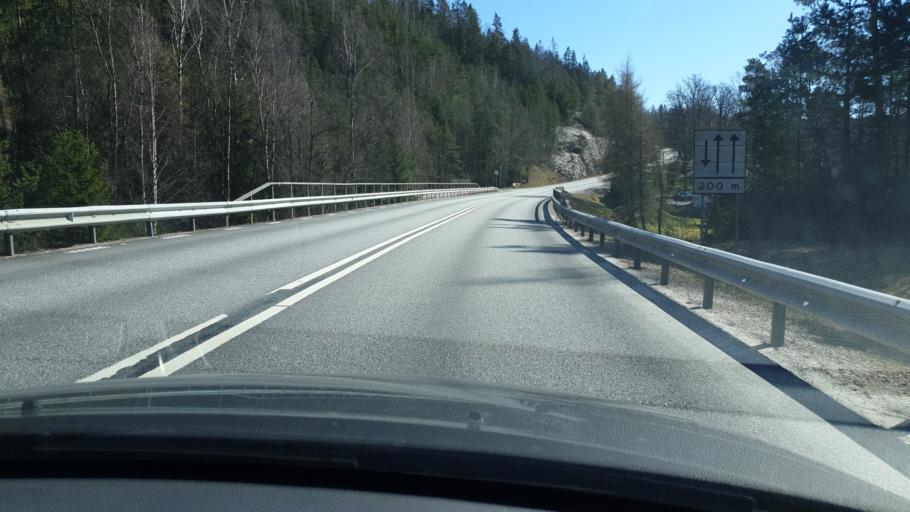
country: SE
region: Vaestra Goetaland
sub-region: Tanums Kommun
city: Tanumshede
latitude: 58.7969
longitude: 11.5689
